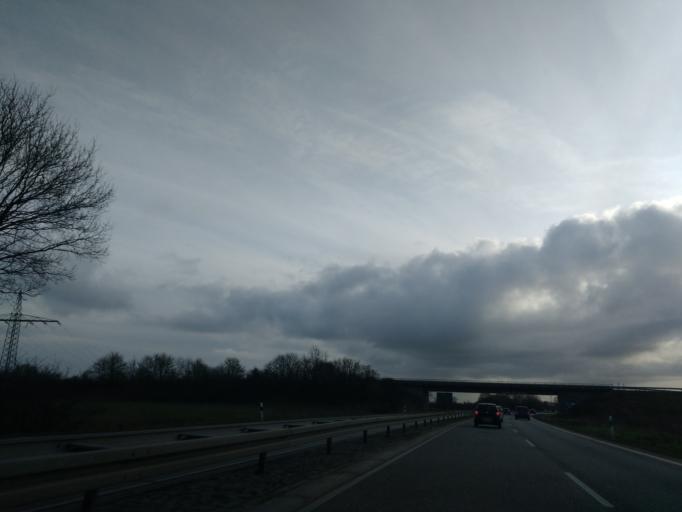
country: DE
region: Schleswig-Holstein
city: Krogaspe
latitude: 54.1187
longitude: 9.9592
